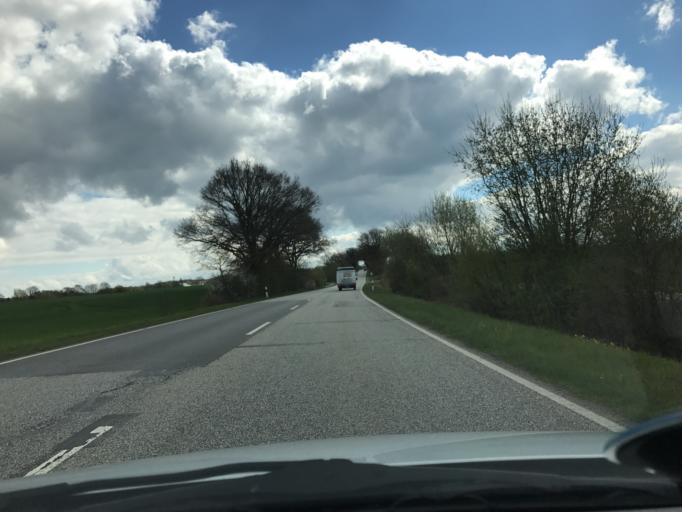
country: DE
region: Schleswig-Holstein
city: Eutin
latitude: 54.1149
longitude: 10.6563
